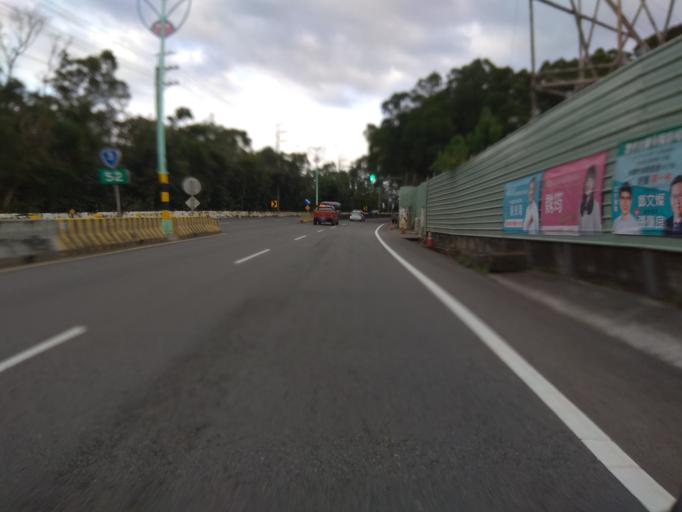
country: TW
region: Taiwan
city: Daxi
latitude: 24.8432
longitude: 121.2113
